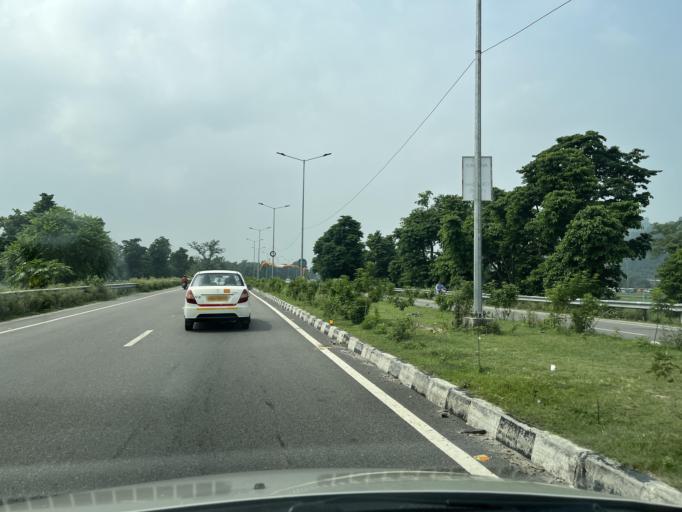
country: IN
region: Uttarakhand
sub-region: Haridwar
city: Haridwar
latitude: 29.9664
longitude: 78.1798
